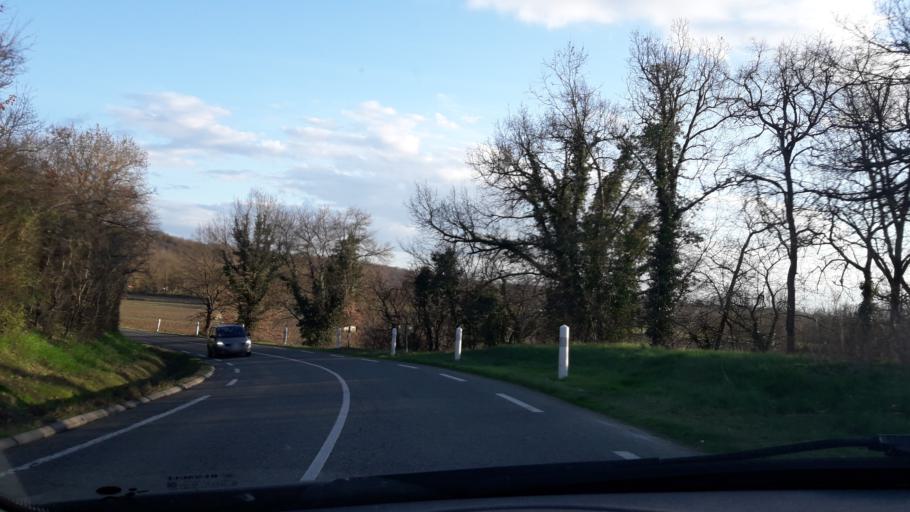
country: FR
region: Midi-Pyrenees
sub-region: Departement de la Haute-Garonne
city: Montaigut-sur-Save
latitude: 43.7227
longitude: 1.2454
